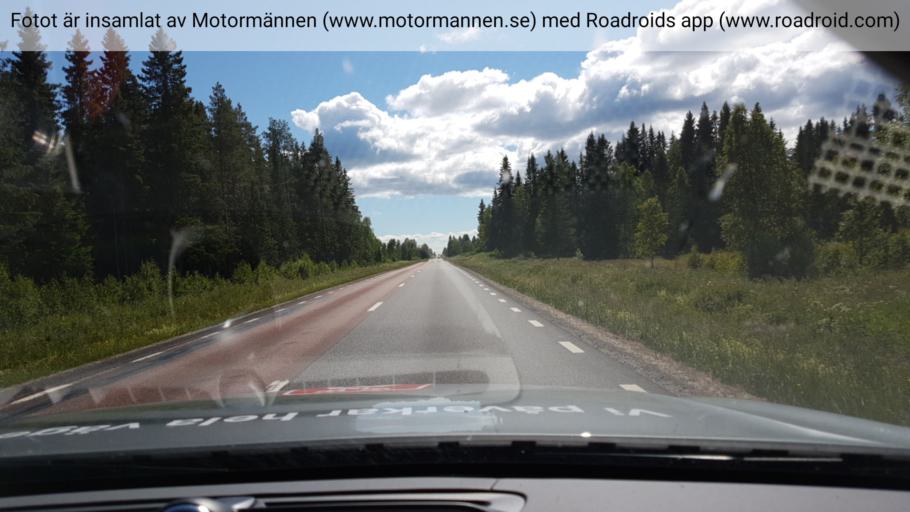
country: SE
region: Jaemtland
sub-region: Stroemsunds Kommun
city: Stroemsund
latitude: 63.7892
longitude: 15.5122
